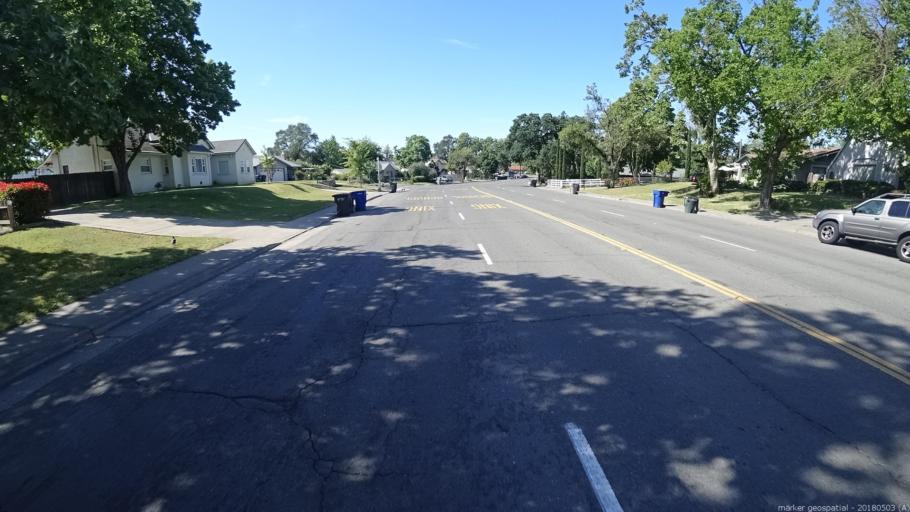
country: US
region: California
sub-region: Sacramento County
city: Arden-Arcade
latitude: 38.6212
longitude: -121.4328
